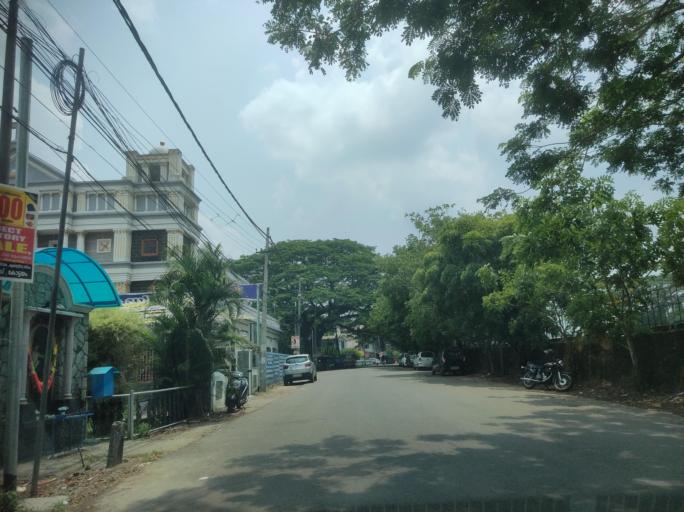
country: IN
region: Kerala
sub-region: Kottayam
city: Kottayam
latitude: 9.5915
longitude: 76.5329
